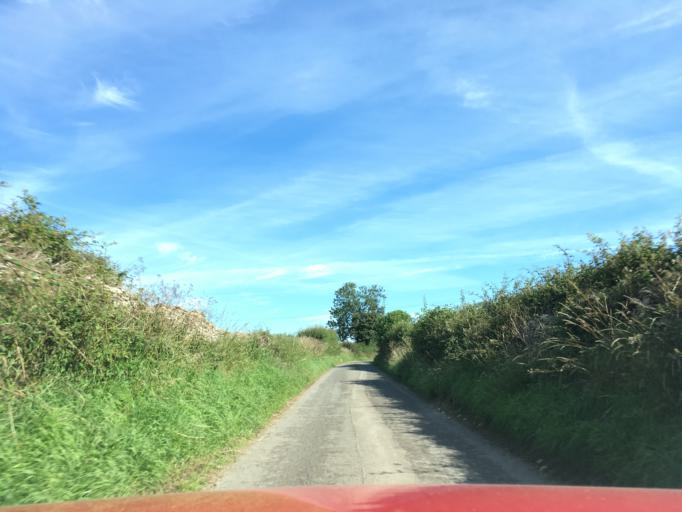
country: GB
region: England
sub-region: Wiltshire
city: Nettleton
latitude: 51.4755
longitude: -2.2643
